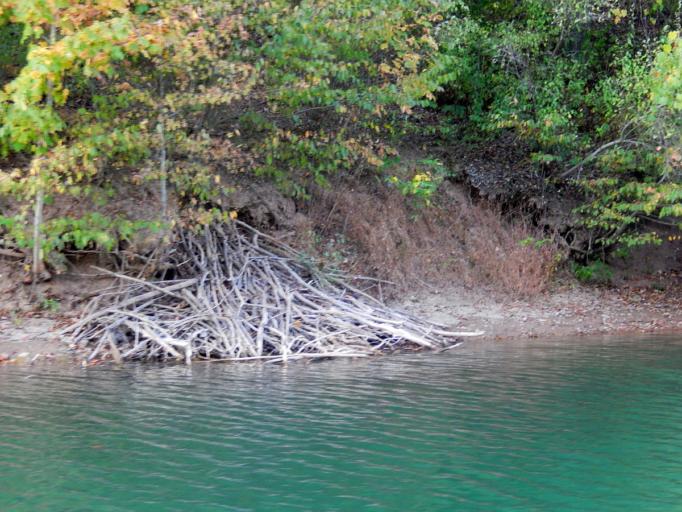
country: US
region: West Virginia
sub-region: Upshur County
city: Buckhannon
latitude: 38.9684
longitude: -80.3294
